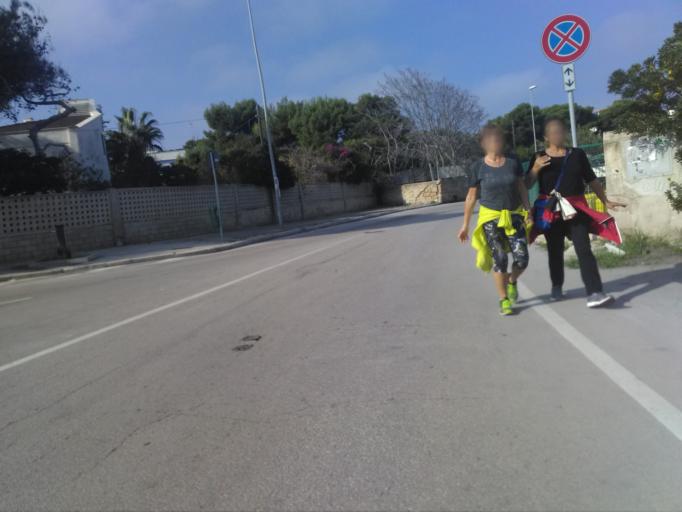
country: IT
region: Apulia
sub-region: Provincia di Bari
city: San Paolo
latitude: 41.1601
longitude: 16.7630
